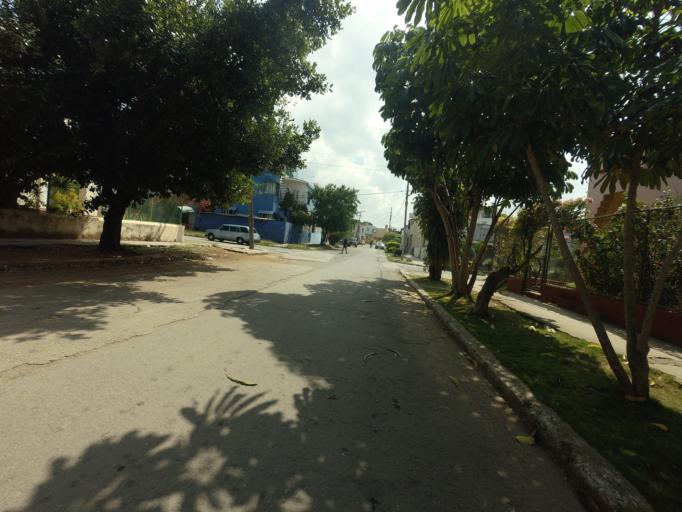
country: CU
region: La Habana
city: Cerro
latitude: 23.1081
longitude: -82.4258
